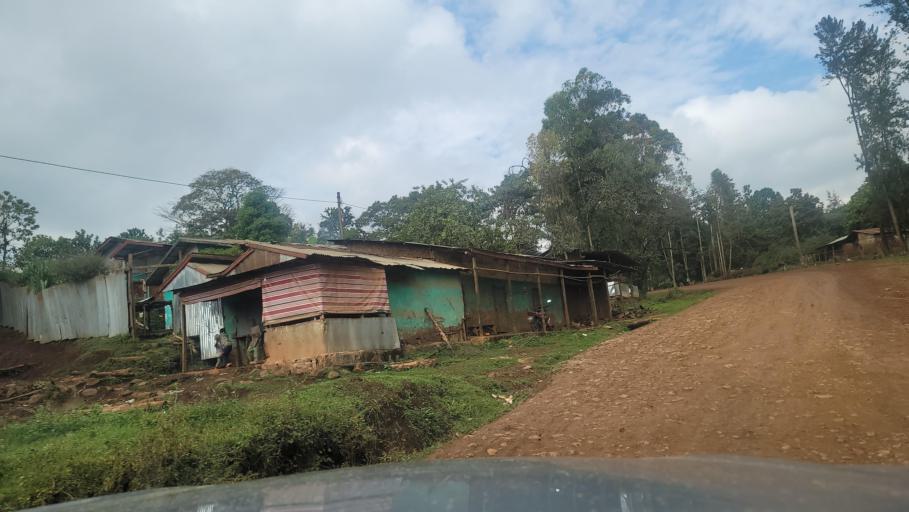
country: ET
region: Oromiya
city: Agaro
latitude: 7.7870
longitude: 36.4244
